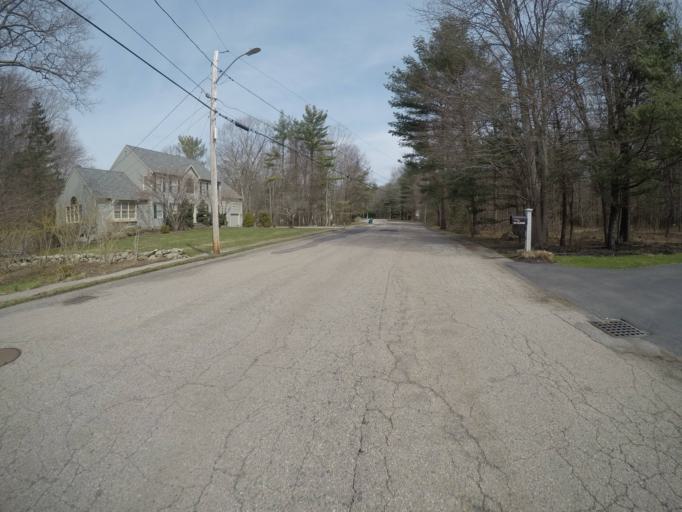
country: US
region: Massachusetts
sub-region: Bristol County
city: Easton
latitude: 42.0421
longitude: -71.1078
